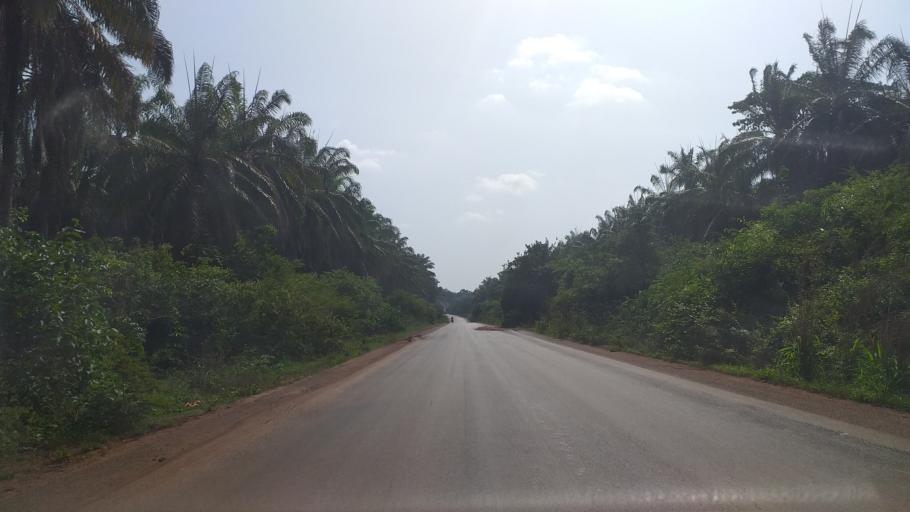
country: GN
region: Boke
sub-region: Boke Prefecture
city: Boke
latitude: 10.8344
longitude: -14.3589
